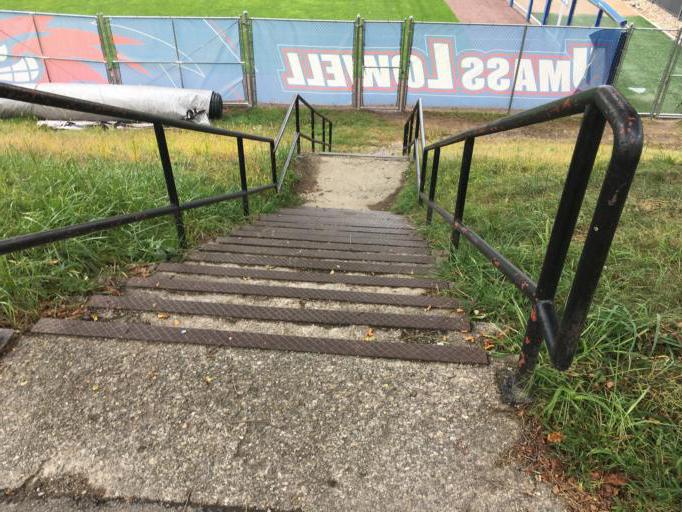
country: US
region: Massachusetts
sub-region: Middlesex County
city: Lowell
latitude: 42.6420
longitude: -71.3359
